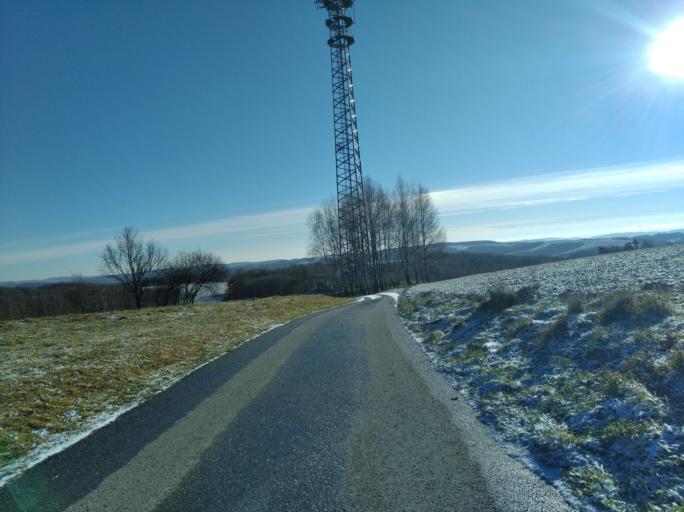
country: PL
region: Subcarpathian Voivodeship
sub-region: Powiat strzyzowski
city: Czudec
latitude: 49.9496
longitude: 21.7621
